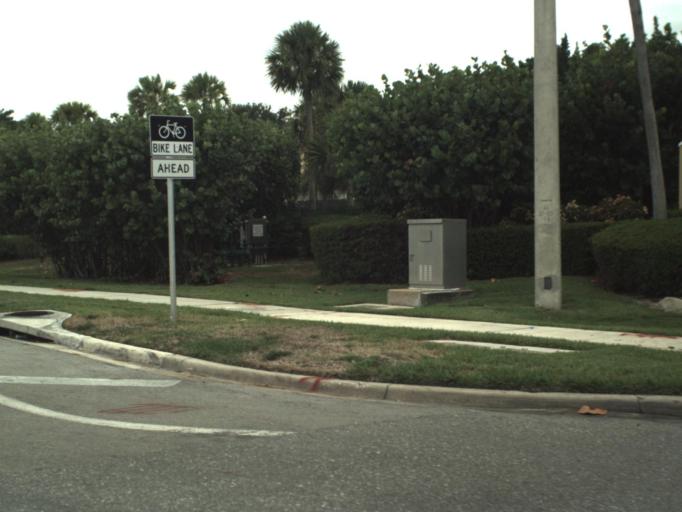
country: US
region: Florida
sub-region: Palm Beach County
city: Jupiter
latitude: 26.9442
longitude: -80.0846
